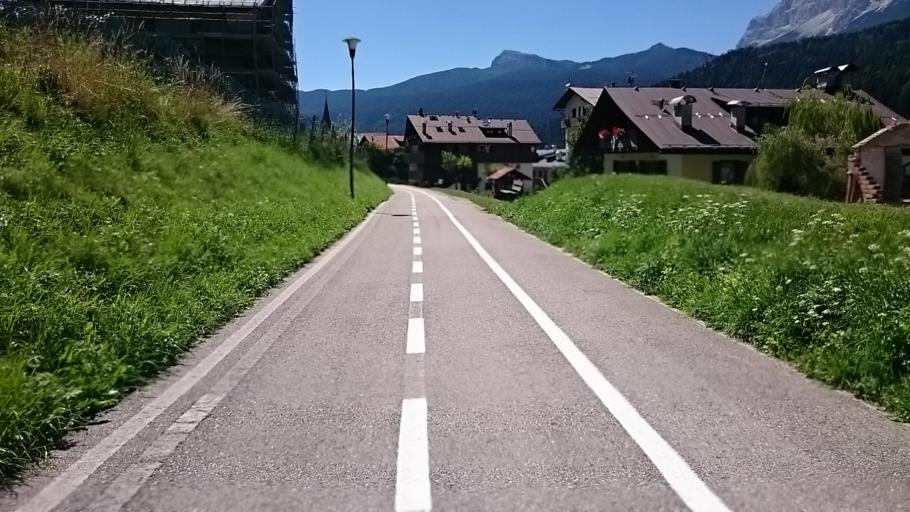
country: IT
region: Veneto
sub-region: Provincia di Belluno
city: San Vito
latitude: 46.4658
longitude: 12.2047
